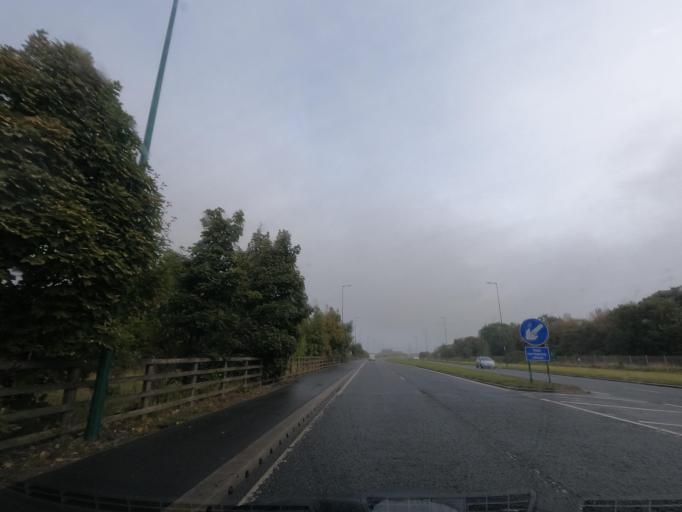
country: GB
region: England
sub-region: Redcar and Cleveland
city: South Bank
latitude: 54.5997
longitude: -1.1198
